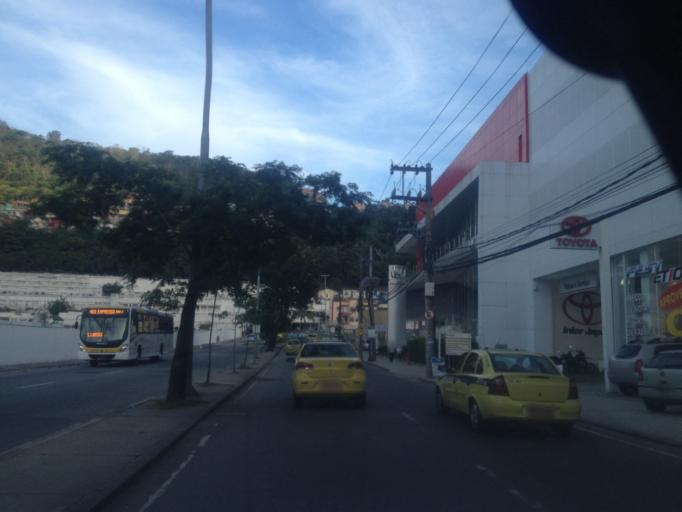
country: BR
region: Rio de Janeiro
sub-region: Rio De Janeiro
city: Rio de Janeiro
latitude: -22.9593
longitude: -43.1910
